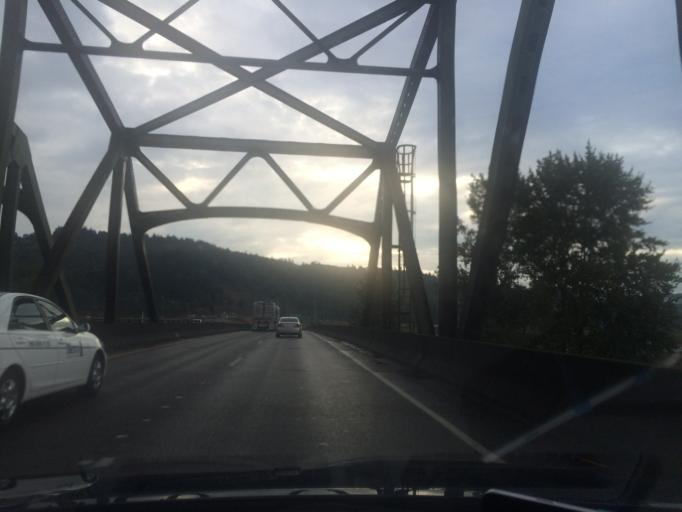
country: US
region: Washington
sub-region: Cowlitz County
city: Kelso
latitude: 46.1067
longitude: -122.8912
